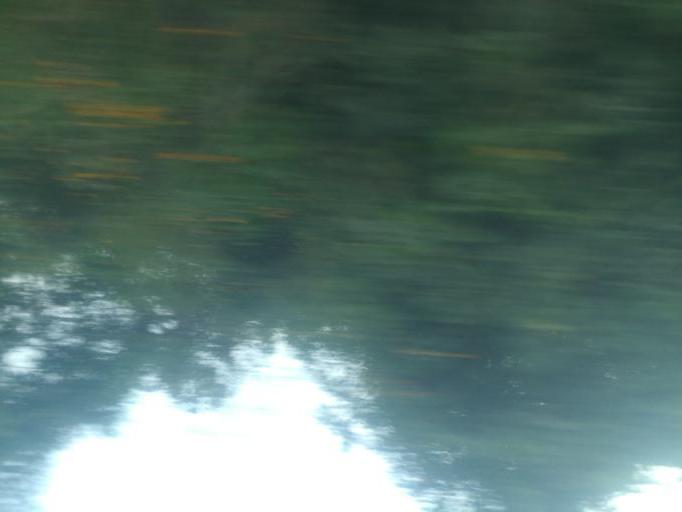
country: NG
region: Ogun
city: Abeokuta
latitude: 7.1472
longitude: 3.2572
